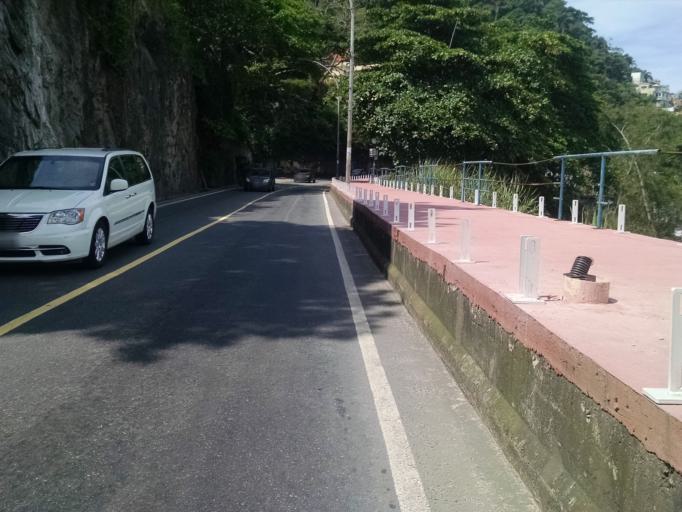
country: BR
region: Rio de Janeiro
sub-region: Rio De Janeiro
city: Rio de Janeiro
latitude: -22.9986
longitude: -43.2402
